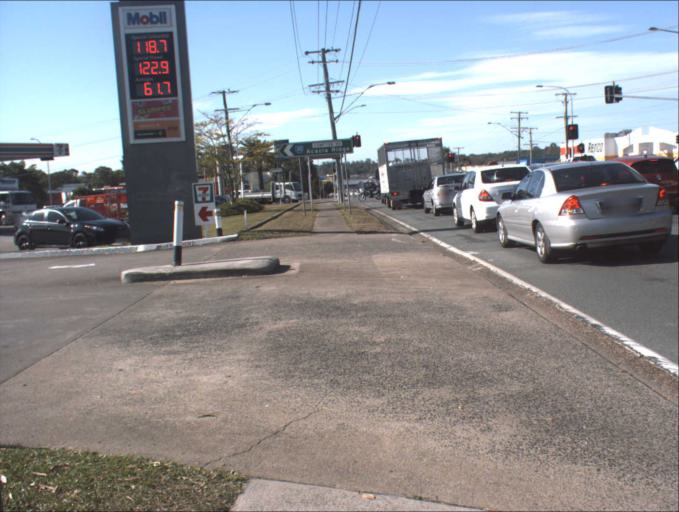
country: AU
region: Queensland
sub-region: Logan
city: Springwood
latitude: -27.6210
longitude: 153.1157
